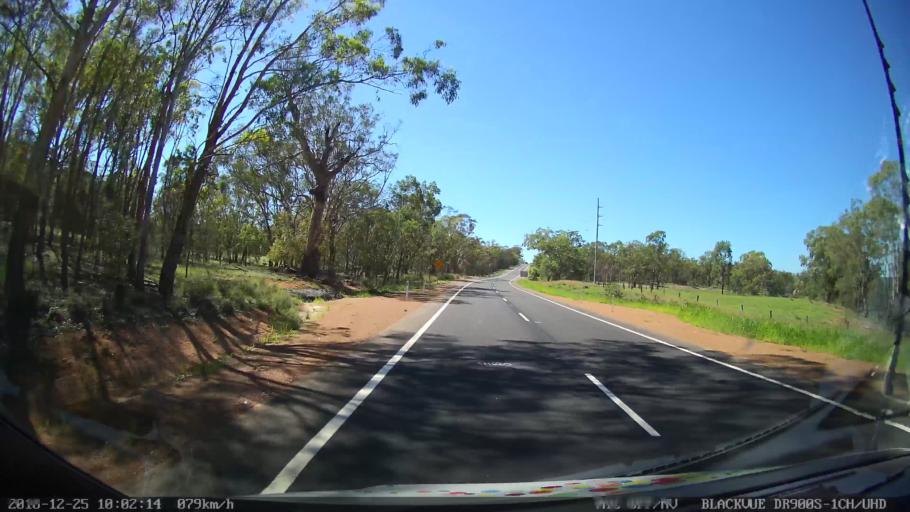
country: AU
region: New South Wales
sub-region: Upper Hunter Shire
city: Merriwa
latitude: -32.2162
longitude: 150.4624
